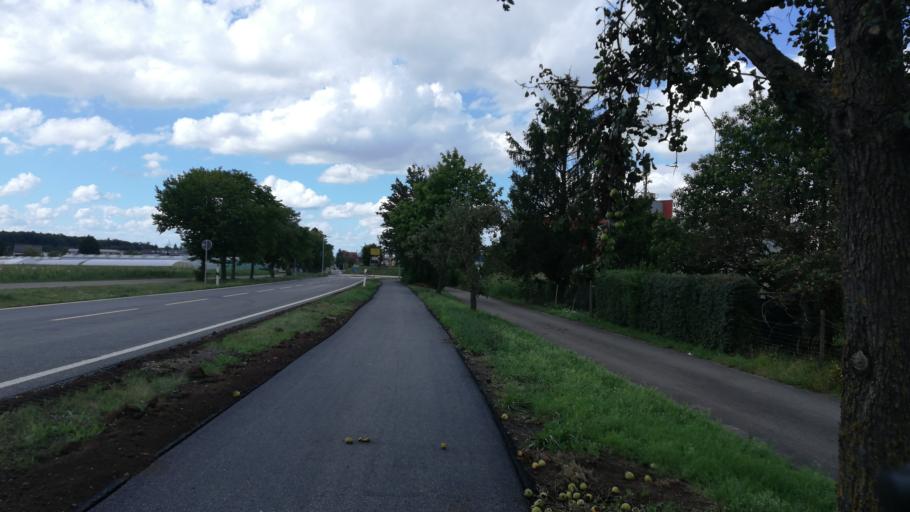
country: DE
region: Baden-Wuerttemberg
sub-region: Regierungsbezirk Stuttgart
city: Waiblingen
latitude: 48.8500
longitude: 9.2997
